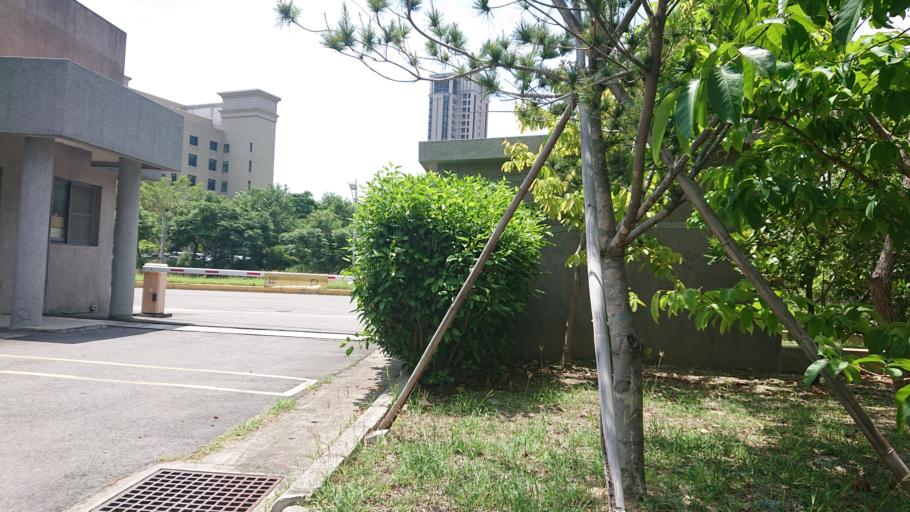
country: TW
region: Taiwan
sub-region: Hsinchu
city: Zhubei
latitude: 24.8139
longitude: 121.0191
